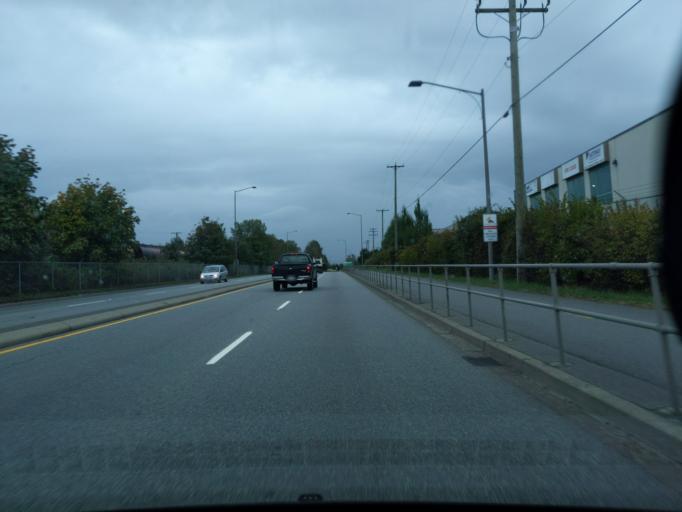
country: CA
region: British Columbia
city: Pitt Meadows
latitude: 49.1807
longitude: -122.7024
